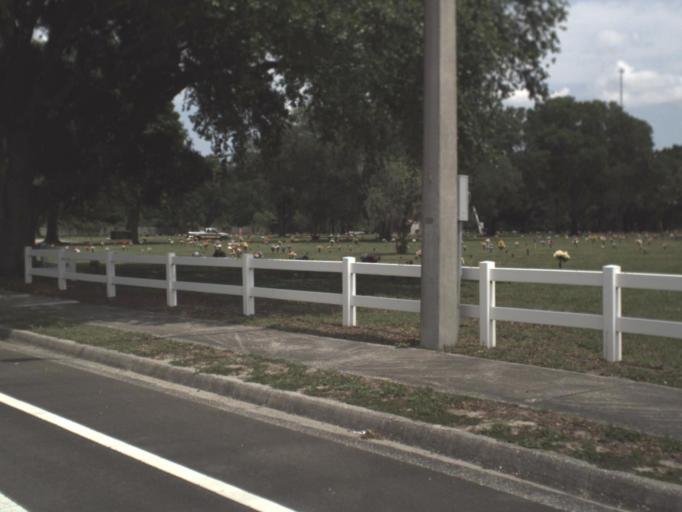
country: US
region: Florida
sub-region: Alachua County
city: Gainesville
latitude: 29.6380
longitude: -82.2783
